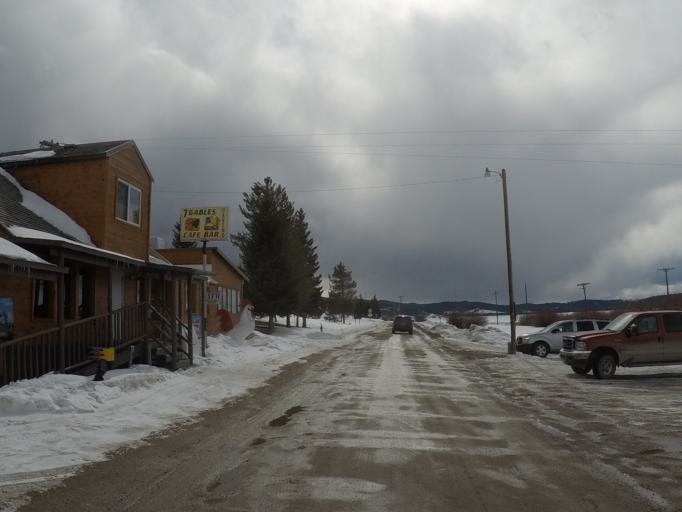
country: US
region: Montana
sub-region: Granite County
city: Philipsburg
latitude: 46.1923
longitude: -113.2631
